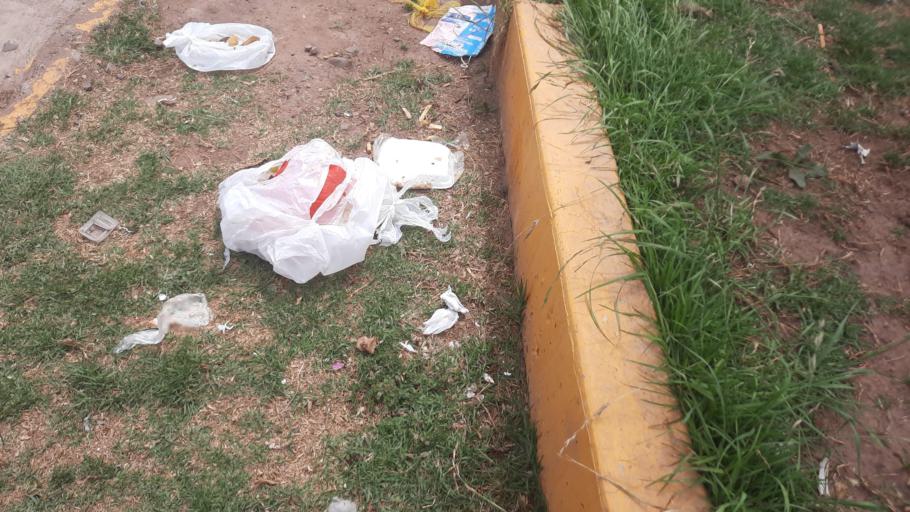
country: PE
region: Cusco
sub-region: Provincia de Cusco
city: Saylla
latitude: -13.5328
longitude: -71.9014
